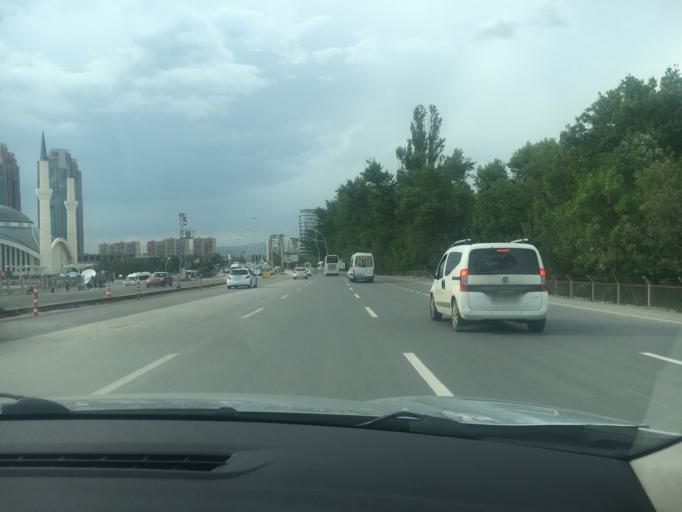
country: TR
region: Ankara
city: Batikent
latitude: 39.9041
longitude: 32.7653
